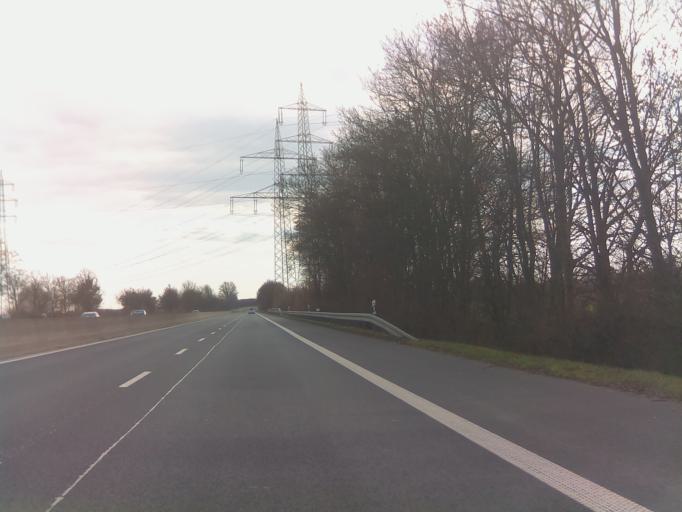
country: DE
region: Hesse
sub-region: Regierungsbezirk Darmstadt
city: Burstadt
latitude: 49.6207
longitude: 8.4593
